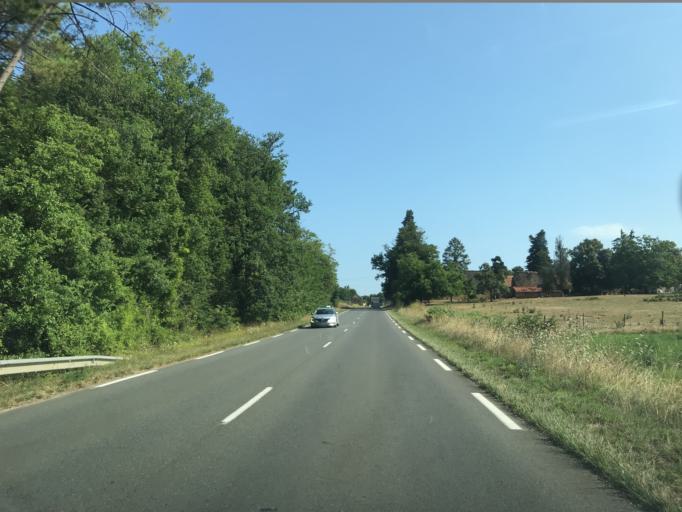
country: FR
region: Aquitaine
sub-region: Departement de la Dordogne
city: Sarlat-la-Caneda
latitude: 44.9851
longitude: 1.2395
